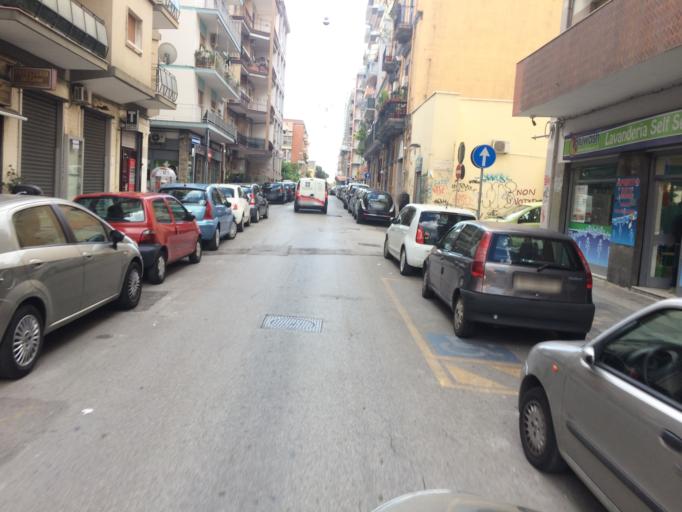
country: IT
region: Apulia
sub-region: Provincia di Bari
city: Bari
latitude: 41.1137
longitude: 16.8723
